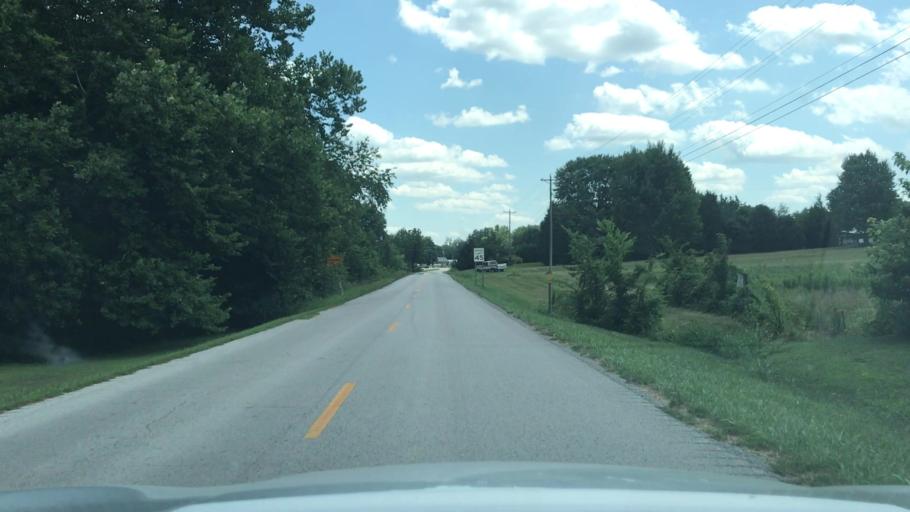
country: US
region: Kentucky
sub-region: Christian County
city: Hopkinsville
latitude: 36.9876
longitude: -87.3601
